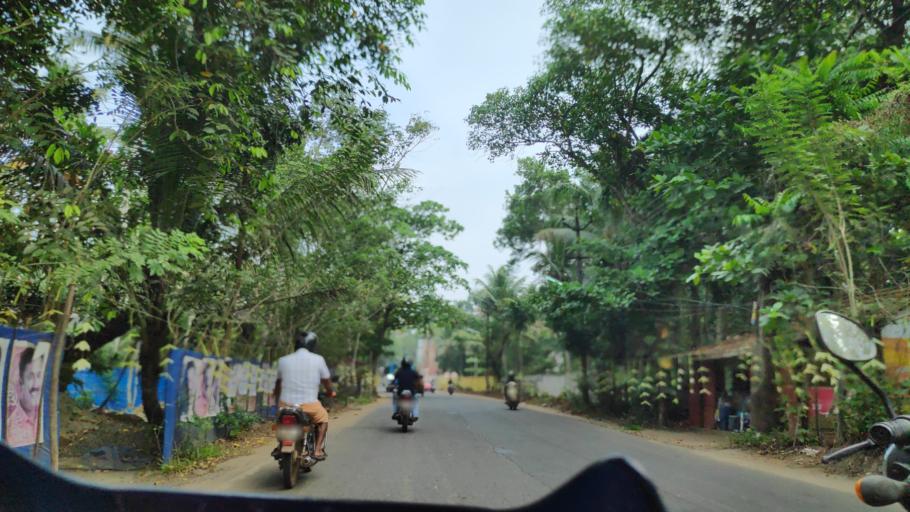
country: IN
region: Kerala
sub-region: Alappuzha
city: Shertallai
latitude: 9.7102
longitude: 76.3577
